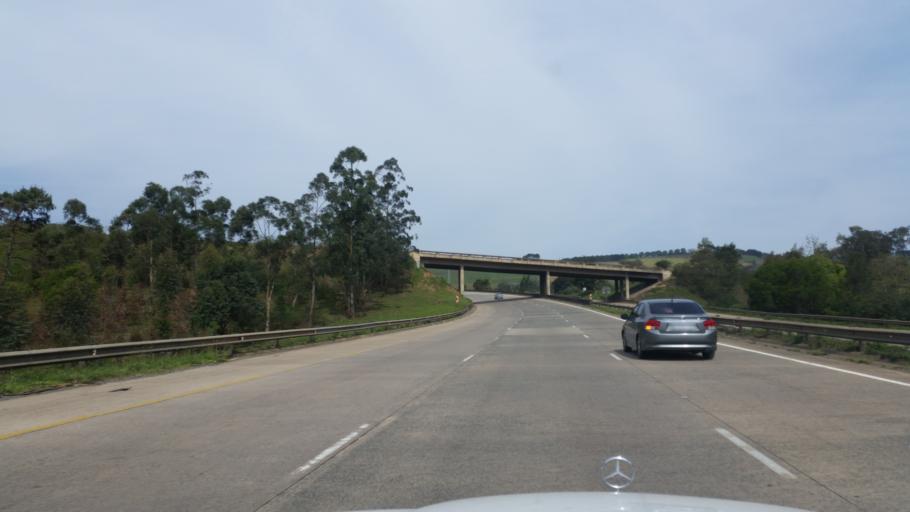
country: ZA
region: KwaZulu-Natal
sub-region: eThekwini Metropolitan Municipality
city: Mpumalanga
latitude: -29.7407
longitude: 30.6245
